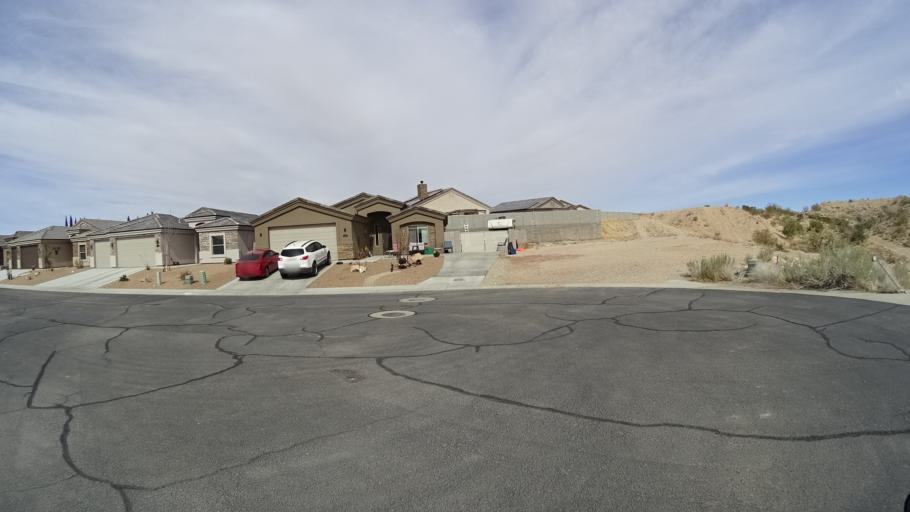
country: US
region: Arizona
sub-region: Mohave County
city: Kingman
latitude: 35.1856
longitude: -114.0162
